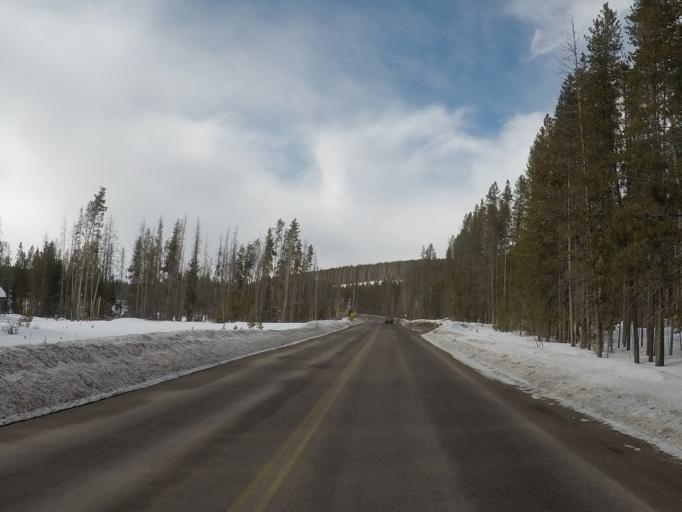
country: US
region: Montana
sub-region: Granite County
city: Philipsburg
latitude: 46.2098
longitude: -113.2741
